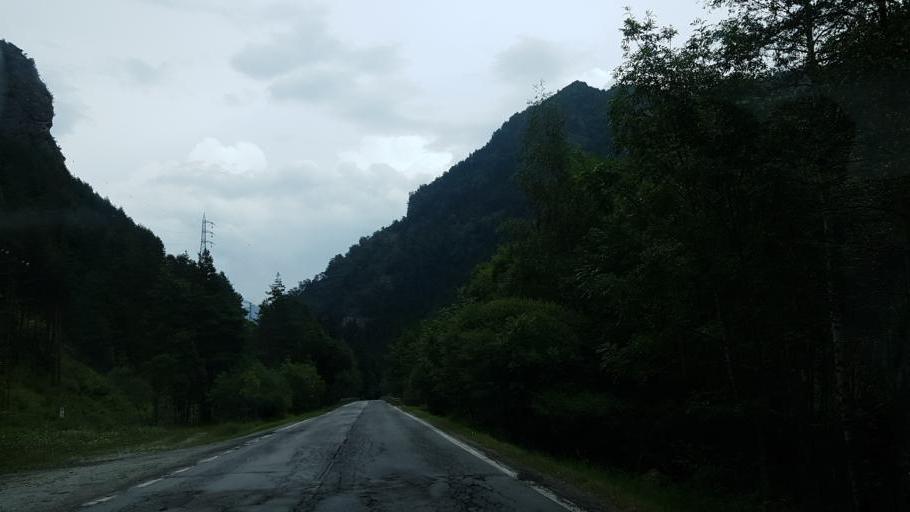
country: IT
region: Piedmont
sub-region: Provincia di Cuneo
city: Marmora
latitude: 44.4883
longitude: 7.0867
